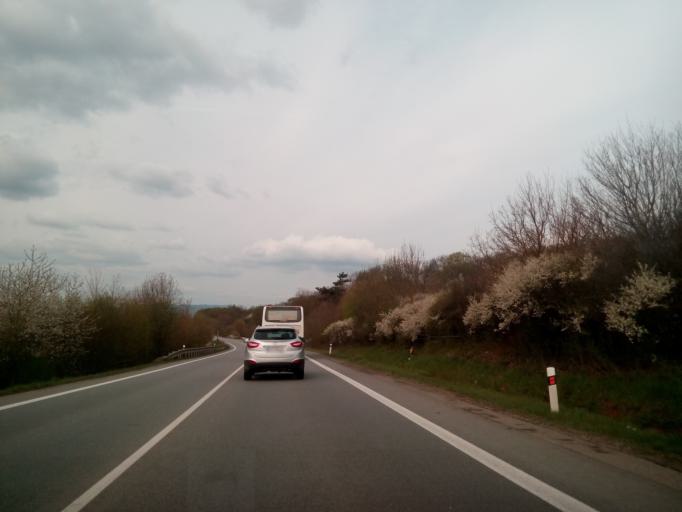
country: SK
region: Kosicky
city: Moldava nad Bodvou
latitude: 48.6076
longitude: 20.9709
